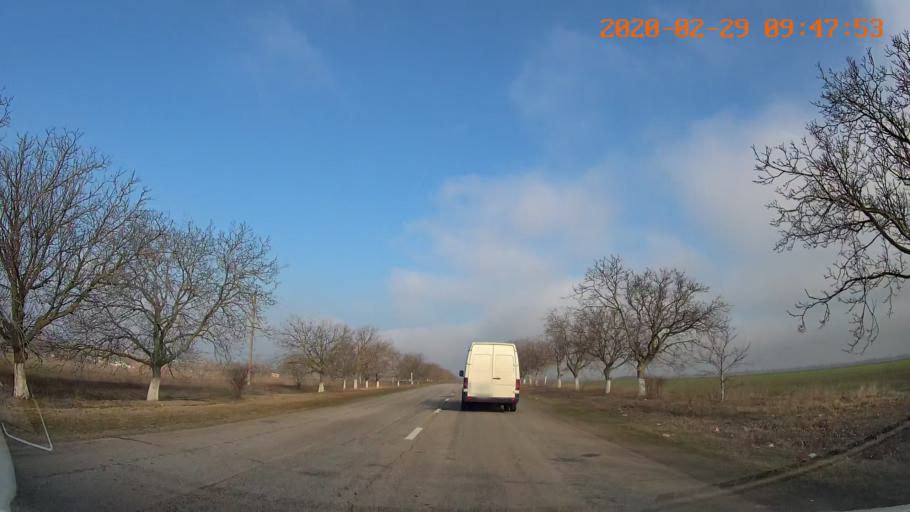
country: MD
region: Telenesti
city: Crasnoe
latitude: 46.6815
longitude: 29.7876
